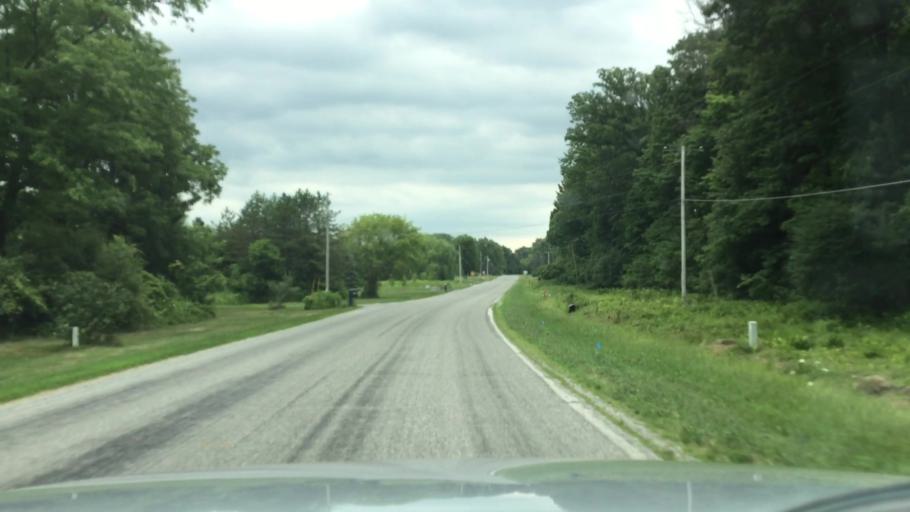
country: US
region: Michigan
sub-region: Saginaw County
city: Birch Run
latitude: 43.3217
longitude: -83.8150
